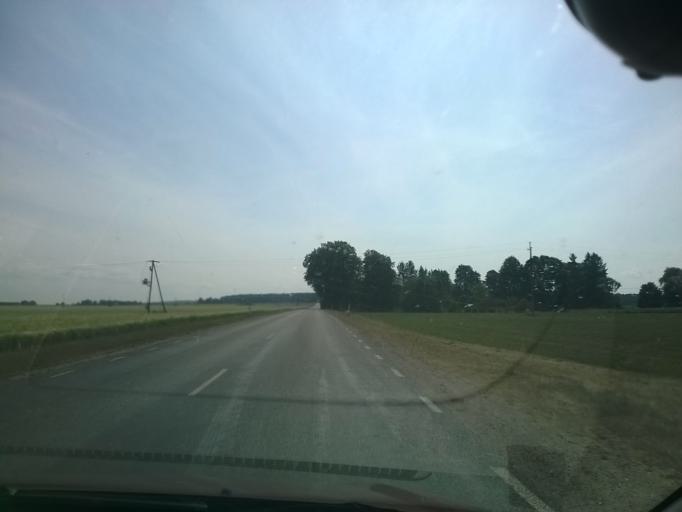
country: EE
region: Tartu
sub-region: Puhja vald
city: Puhja
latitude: 58.2704
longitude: 26.1758
